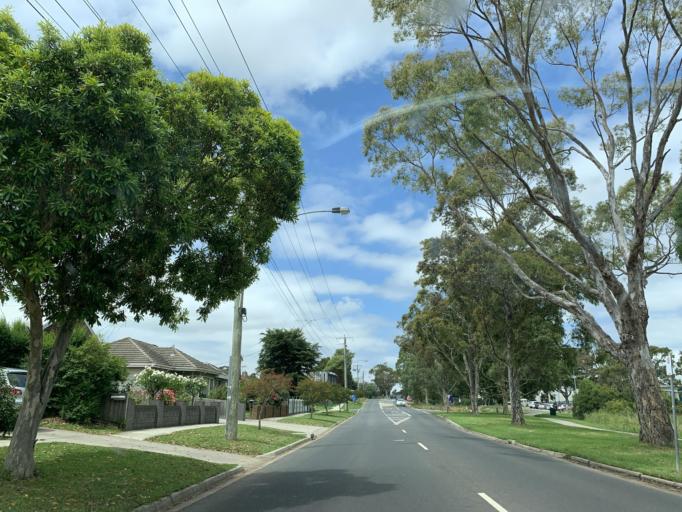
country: AU
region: Victoria
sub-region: Wellington
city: Sale
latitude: -38.1111
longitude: 147.0774
